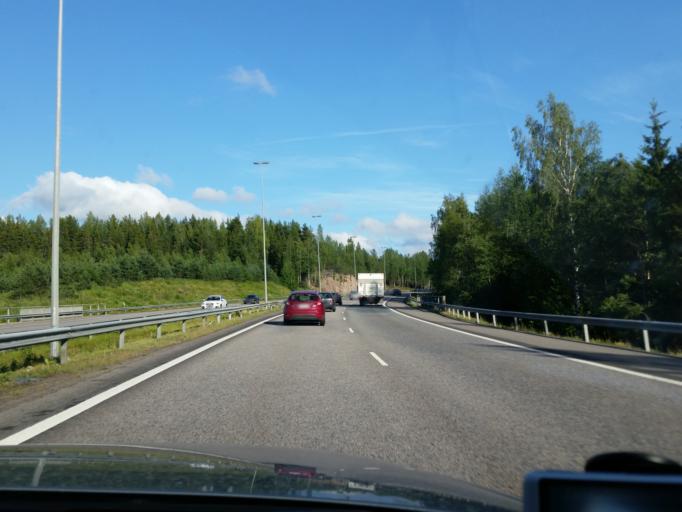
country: FI
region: Uusimaa
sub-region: Helsinki
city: Kirkkonummi
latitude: 60.2811
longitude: 24.4430
